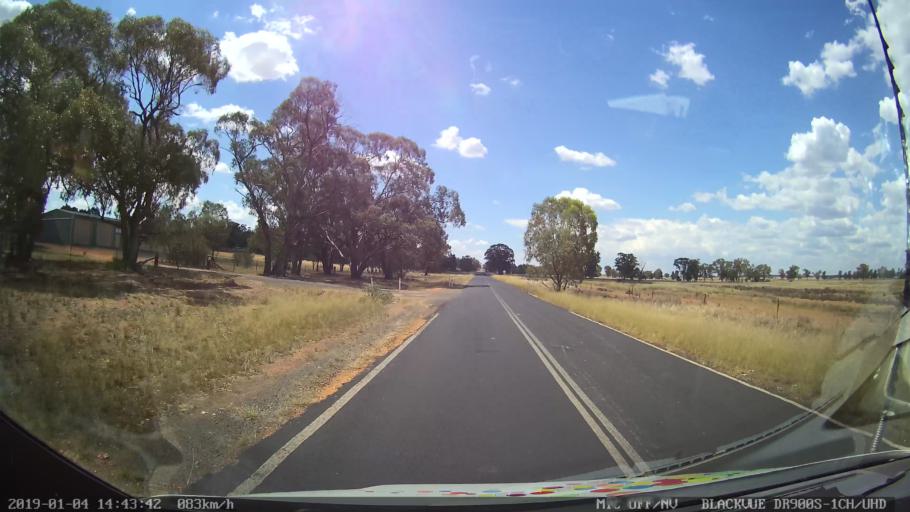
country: AU
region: New South Wales
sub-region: Dubbo Municipality
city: Dubbo
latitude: -32.1157
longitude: 148.6540
